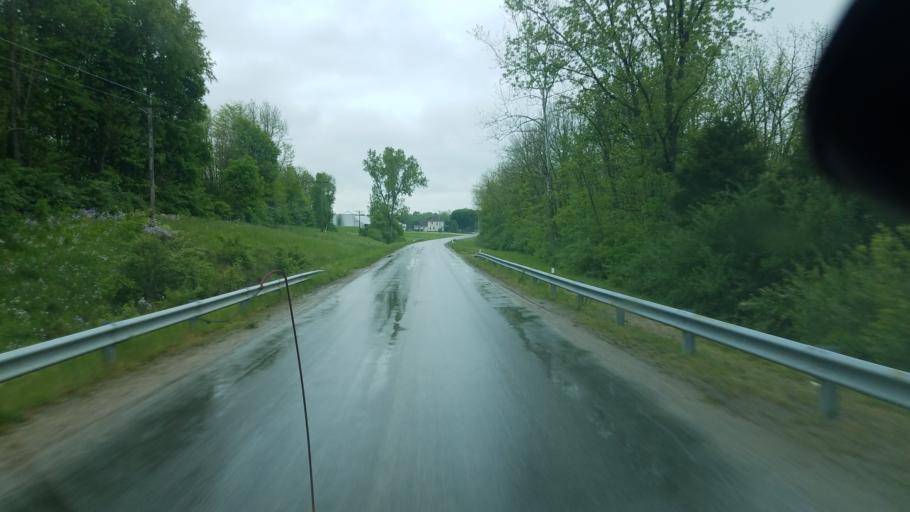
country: US
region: Ohio
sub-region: Highland County
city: Greenfield
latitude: 39.2924
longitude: -83.4621
